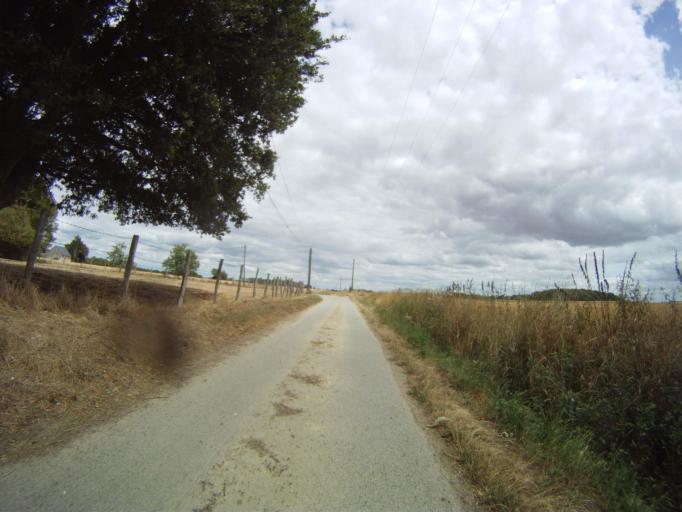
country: FR
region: Centre
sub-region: Departement du Loir-et-Cher
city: Montoire-sur-le-Loir
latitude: 47.6909
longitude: 0.7951
